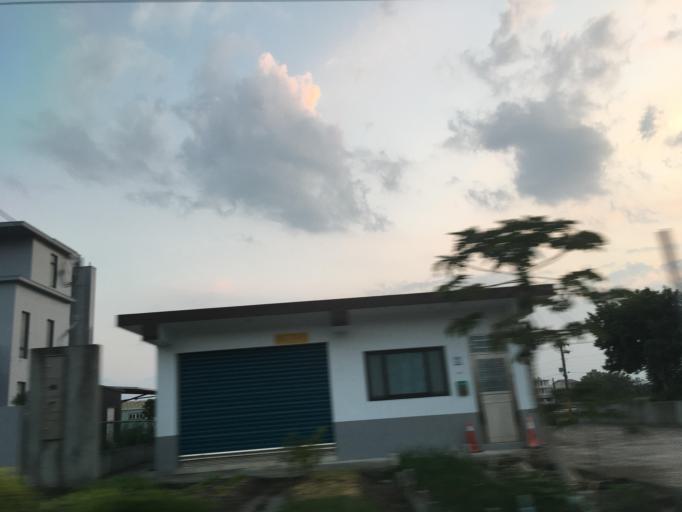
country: TW
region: Taiwan
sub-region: Yilan
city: Yilan
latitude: 24.6926
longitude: 121.7812
